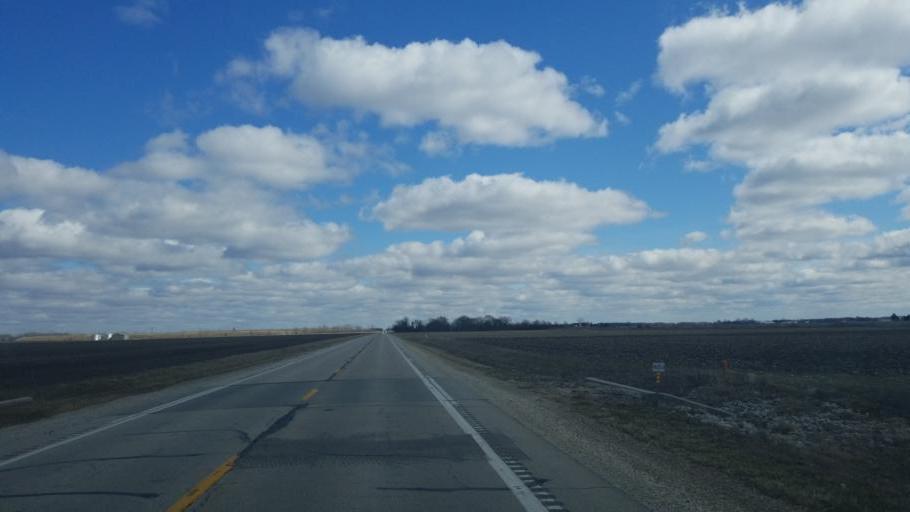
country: US
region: Illinois
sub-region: Douglas County
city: Villa Grove
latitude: 39.7921
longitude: -88.0752
